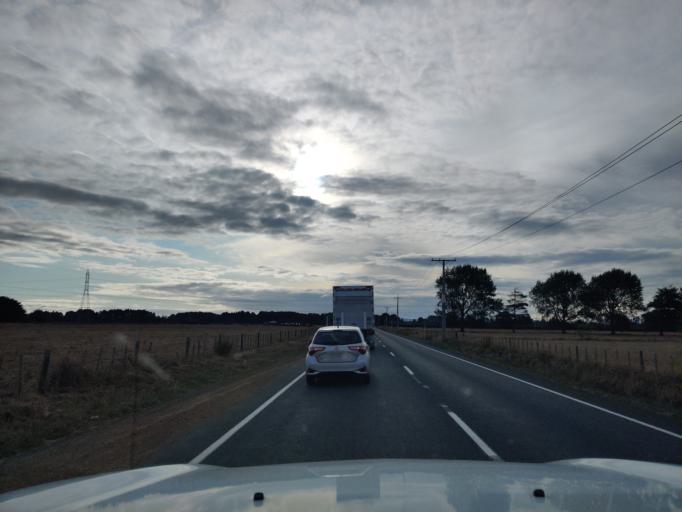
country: NZ
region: Waikato
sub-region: Hamilton City
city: Hamilton
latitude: -37.6863
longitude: 175.3373
